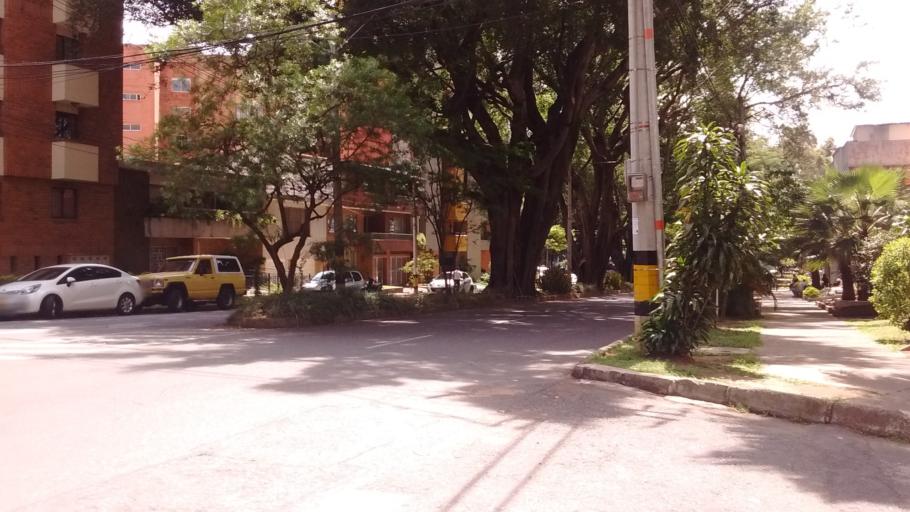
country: CO
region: Antioquia
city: Medellin
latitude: 6.2441
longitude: -75.5979
